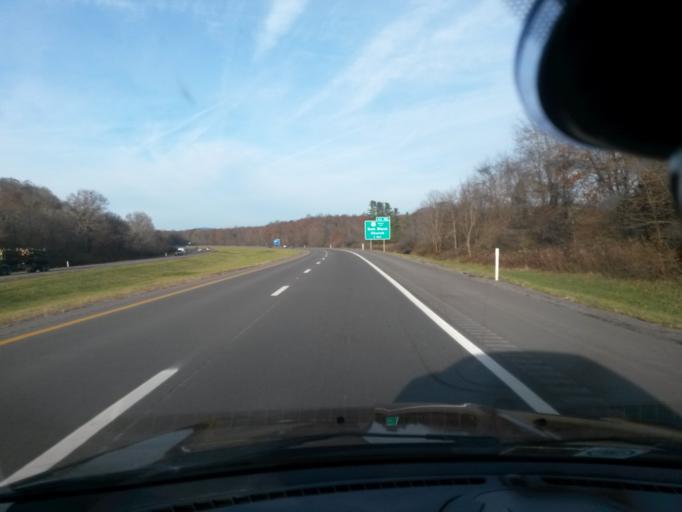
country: US
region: West Virginia
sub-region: Greenbrier County
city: Rainelle
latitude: 37.9073
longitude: -80.6104
